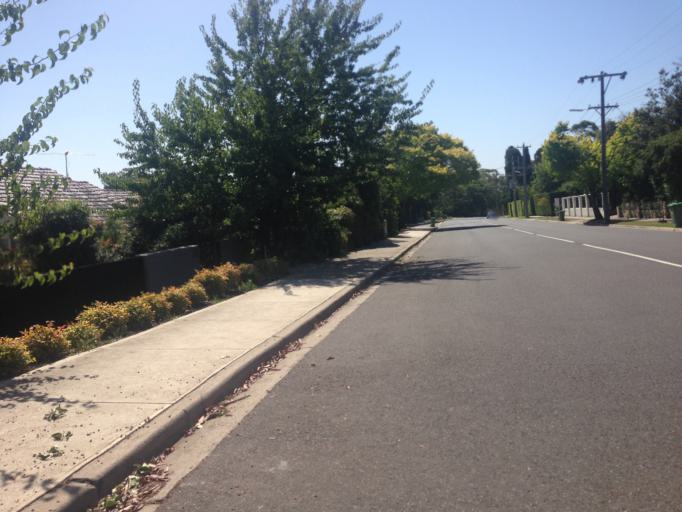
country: AU
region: Victoria
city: Ivanhoe East
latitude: -37.7772
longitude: 145.0552
